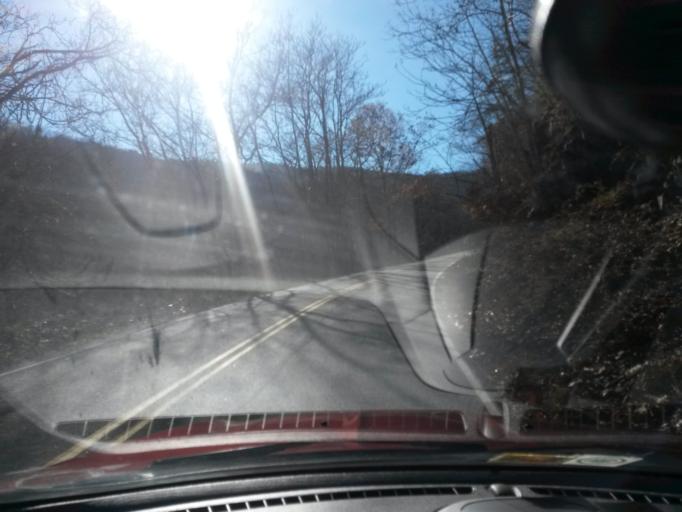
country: US
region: Virginia
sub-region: Botetourt County
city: Buchanan
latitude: 37.4952
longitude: -79.6582
